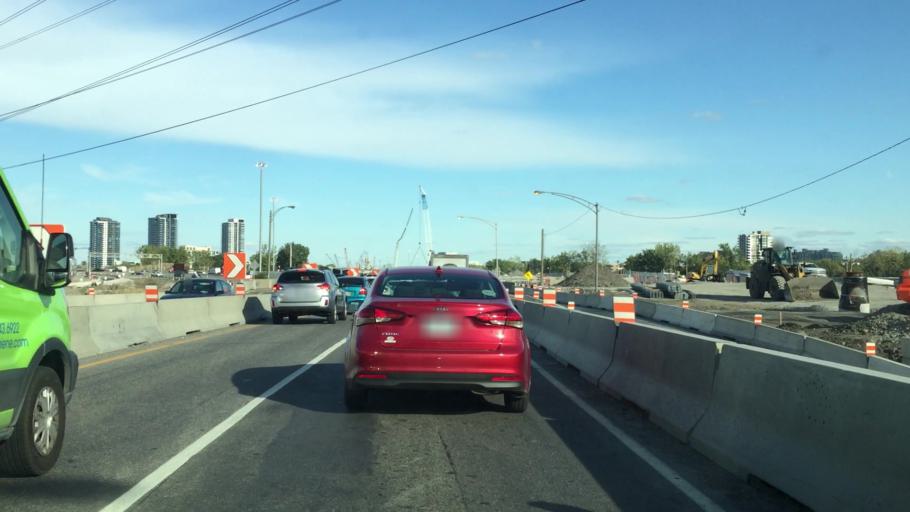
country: CA
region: Quebec
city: Westmount
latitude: 45.4716
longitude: -73.5592
